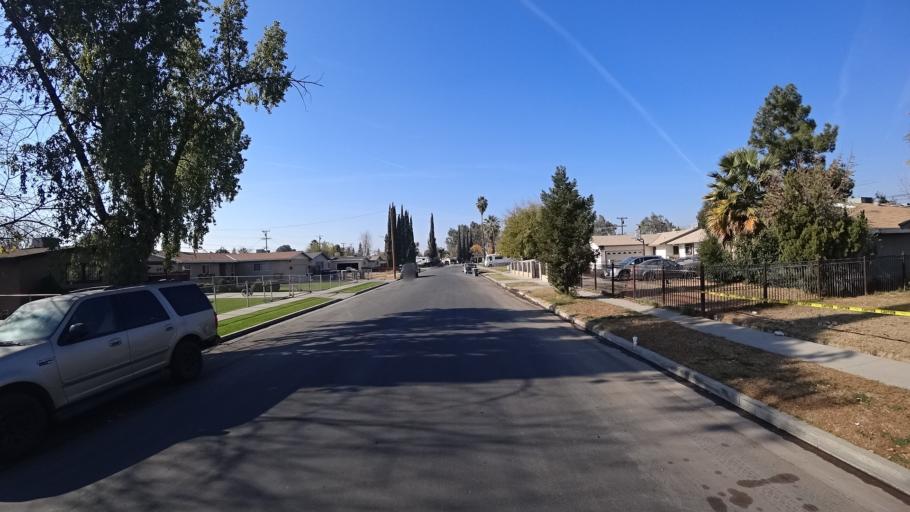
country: US
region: California
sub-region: Kern County
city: Bakersfield
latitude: 35.3231
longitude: -119.0169
